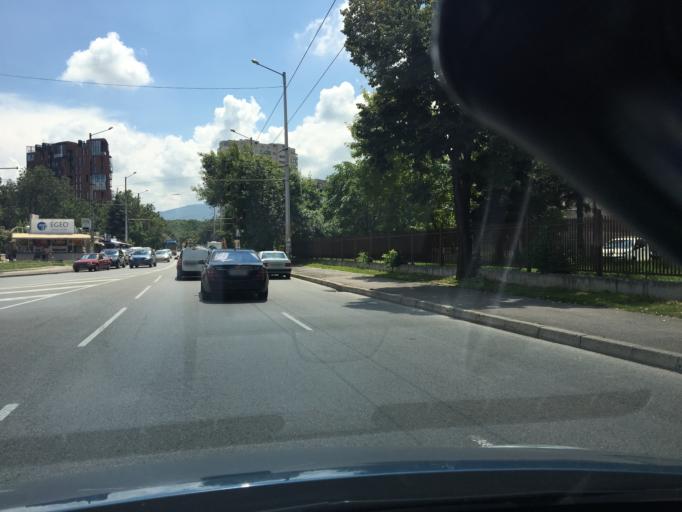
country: BG
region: Sofia-Capital
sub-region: Stolichna Obshtina
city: Sofia
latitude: 42.6772
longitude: 23.3030
